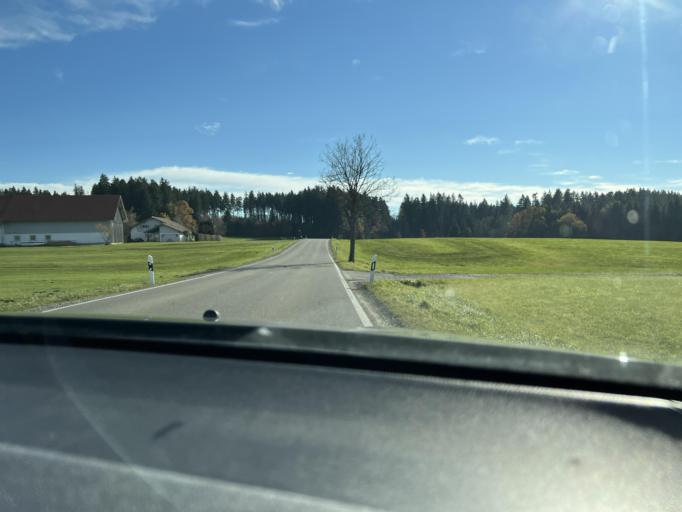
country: DE
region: Bavaria
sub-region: Swabia
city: Gestratz
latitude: 47.7183
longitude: 9.9655
